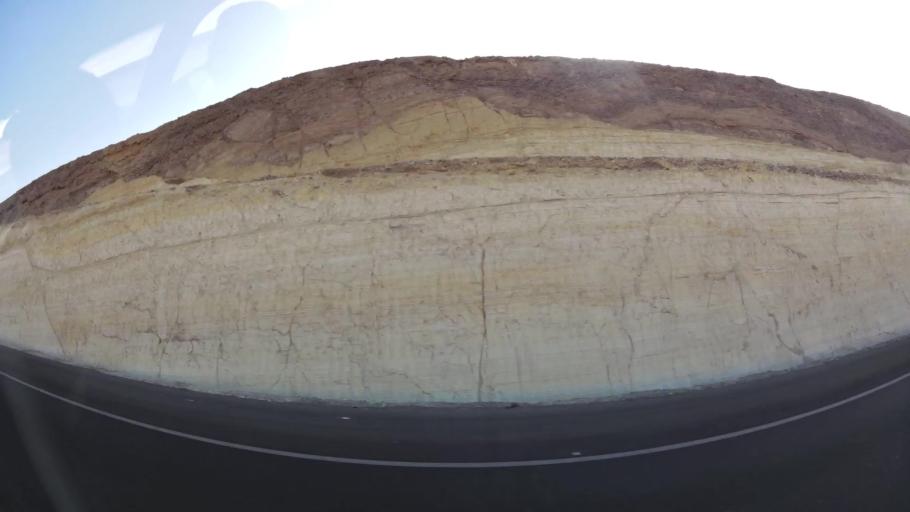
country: PE
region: Ica
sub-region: Provincia de Pisco
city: San Clemente
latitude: -13.6393
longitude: -76.1733
